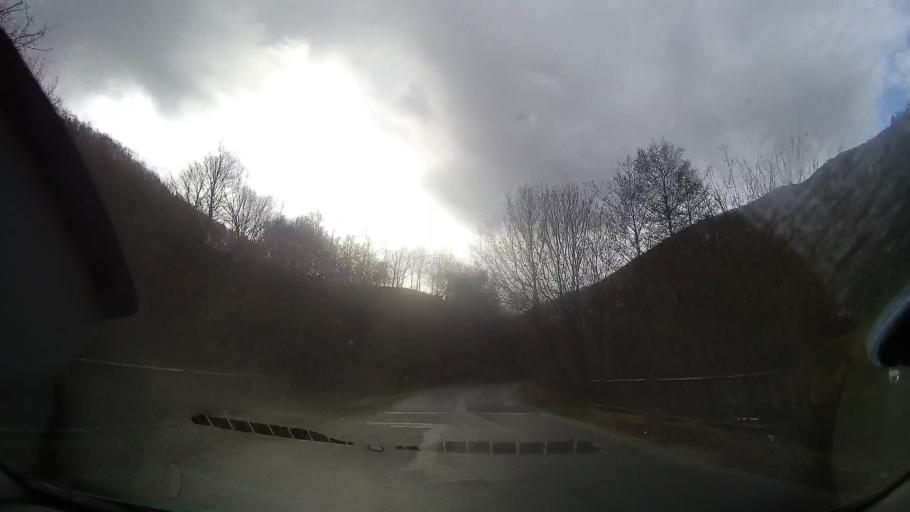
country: RO
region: Alba
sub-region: Comuna Rimetea
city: Rimetea
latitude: 46.4966
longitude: 23.5838
